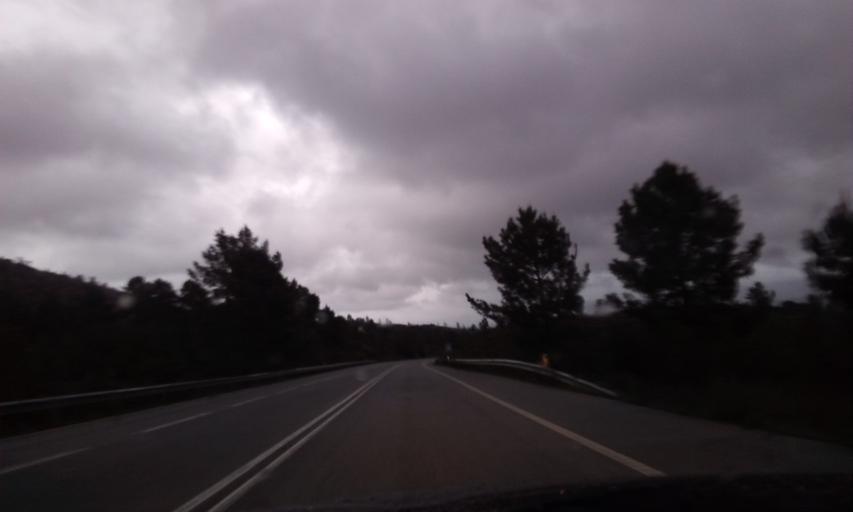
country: PT
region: Guarda
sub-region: Fornos de Algodres
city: Fornos de Algodres
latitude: 40.6035
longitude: -7.5664
